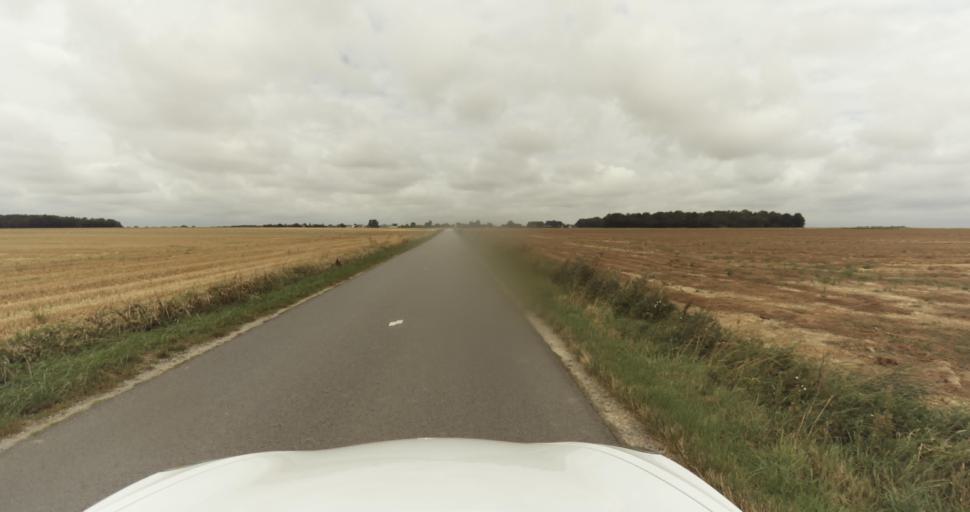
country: FR
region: Haute-Normandie
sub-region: Departement de l'Eure
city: Claville
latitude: 49.0357
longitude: 1.0277
